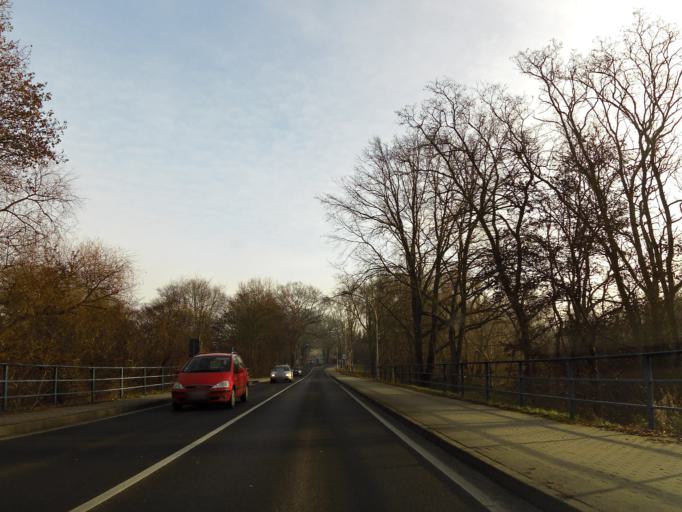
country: DE
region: Brandenburg
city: Werder
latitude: 52.3623
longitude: 12.9453
